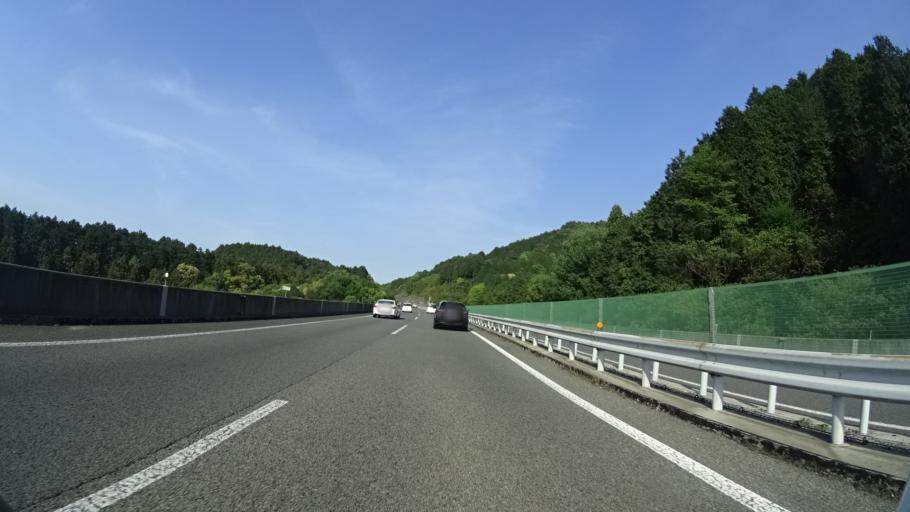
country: JP
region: Ehime
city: Niihama
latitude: 33.9101
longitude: 133.2639
